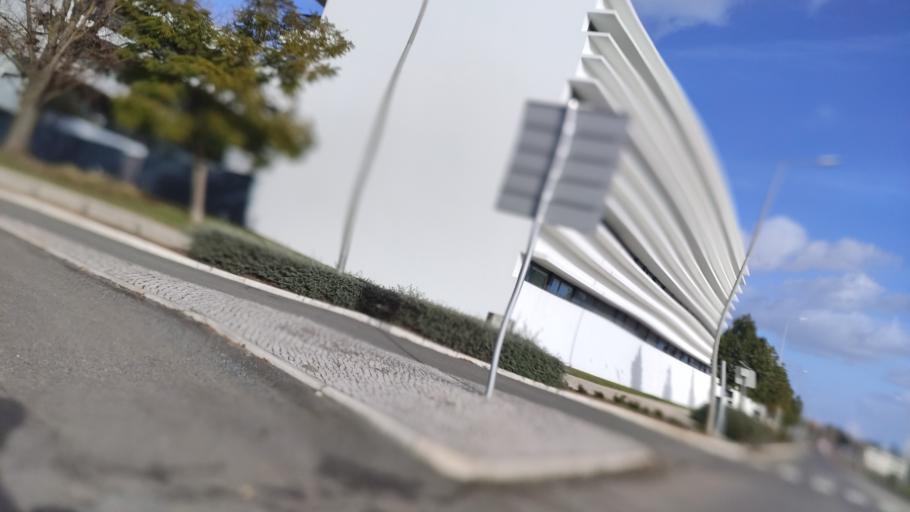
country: PT
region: Beja
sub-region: Beja
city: Beja
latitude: 38.0054
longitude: -7.8626
